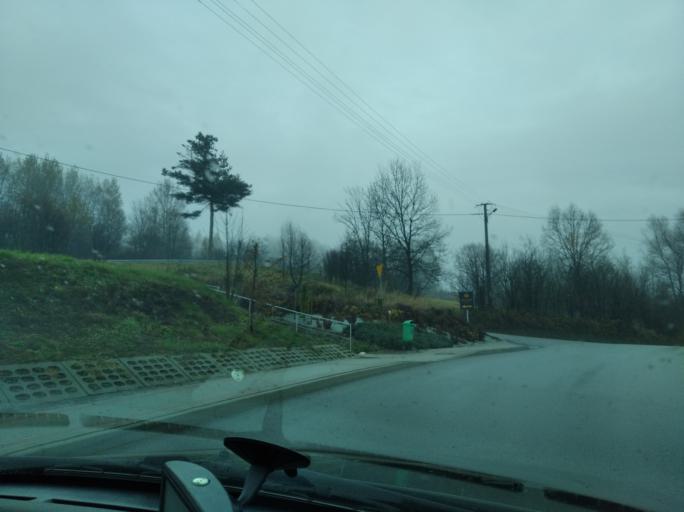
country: PL
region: Subcarpathian Voivodeship
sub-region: Powiat rzeszowski
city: Lubenia
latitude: 49.9304
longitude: 21.9261
